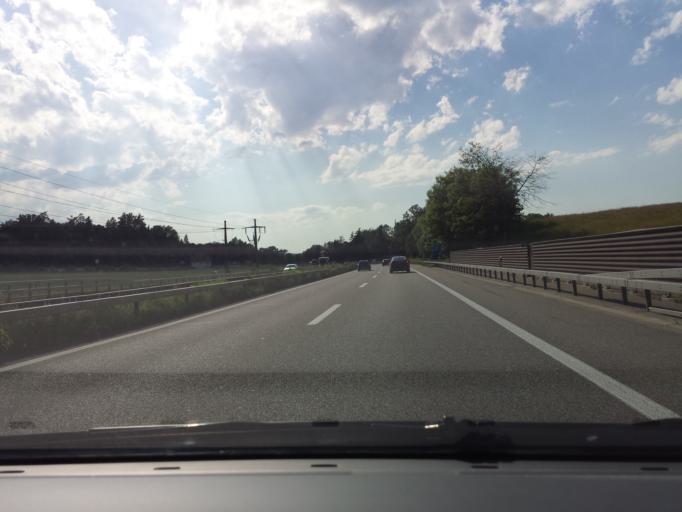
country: CH
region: Saint Gallen
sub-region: Wahlkreis Rorschach
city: Rorschach
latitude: 47.4660
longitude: 9.4811
